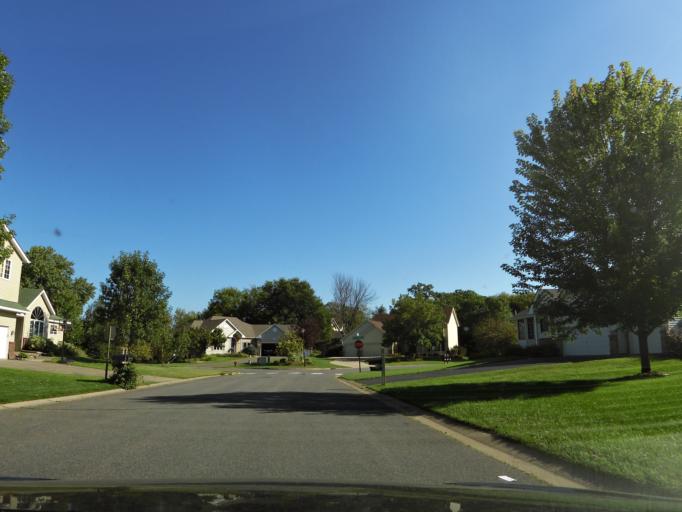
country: US
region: Minnesota
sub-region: Scott County
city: Savage
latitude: 44.7307
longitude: -93.3431
